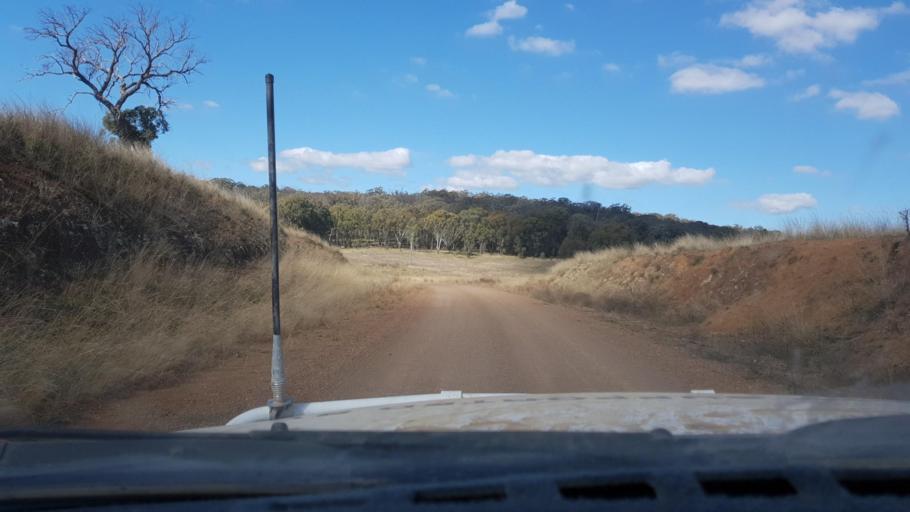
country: AU
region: New South Wales
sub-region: Tamworth Municipality
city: Manilla
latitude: -30.4436
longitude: 150.8647
